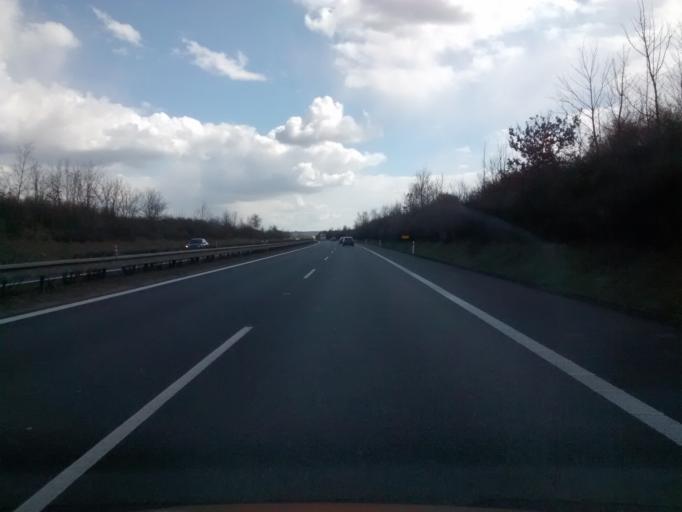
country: CZ
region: Central Bohemia
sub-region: Okres Melnik
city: Veltrusy
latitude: 50.2706
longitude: 14.3595
